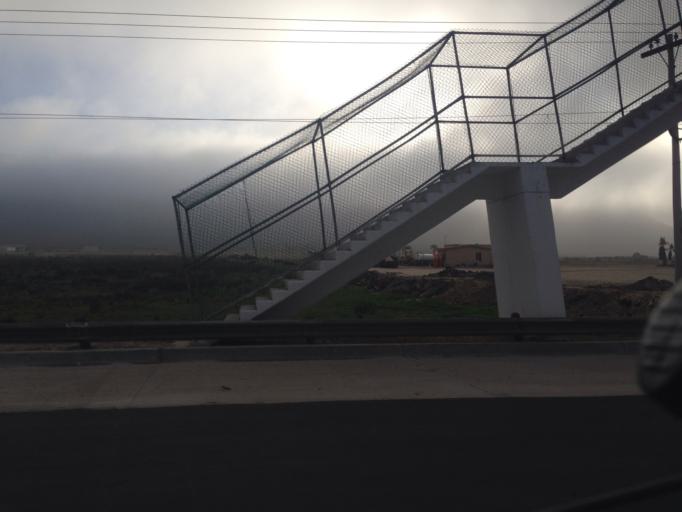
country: MX
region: Baja California
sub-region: Playas de Rosarito
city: Santa Anita
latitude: 32.0681
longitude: -116.8775
